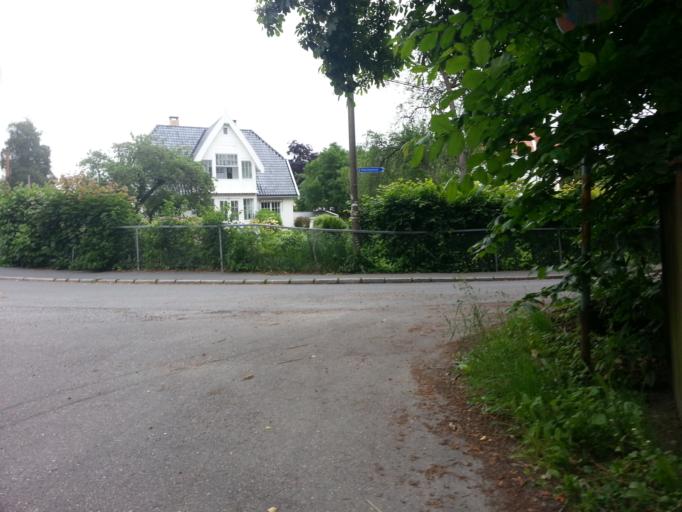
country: NO
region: Oslo
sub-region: Oslo
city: Sjolyststranda
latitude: 59.9355
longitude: 10.6992
